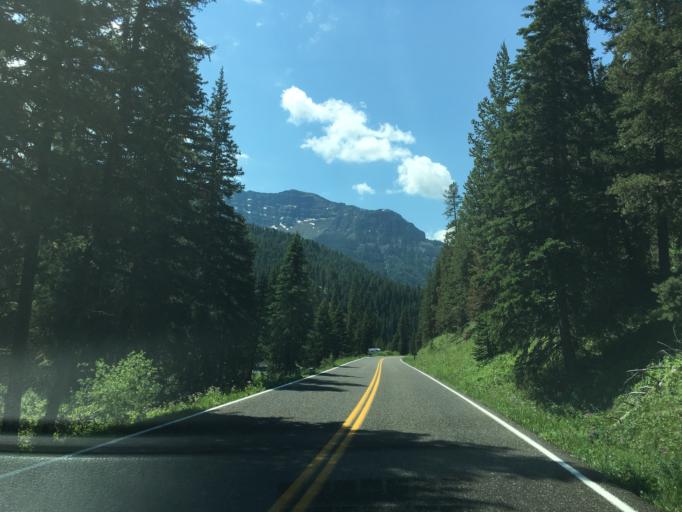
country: US
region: Montana
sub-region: Stillwater County
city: Absarokee
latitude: 44.9368
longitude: -110.0839
